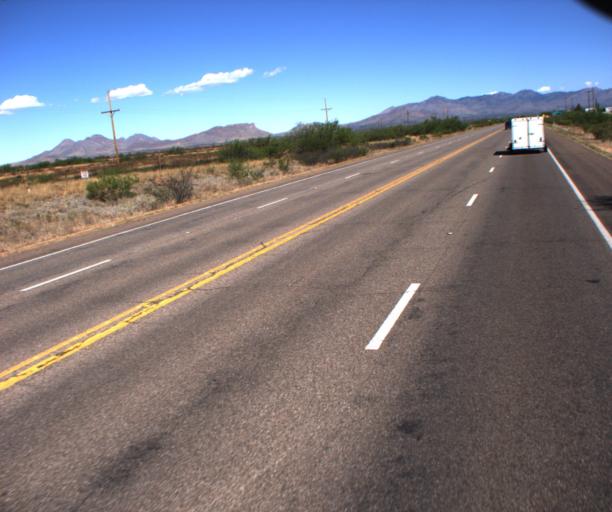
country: US
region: Arizona
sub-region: Cochise County
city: Huachuca City
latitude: 31.6122
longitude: -110.3327
